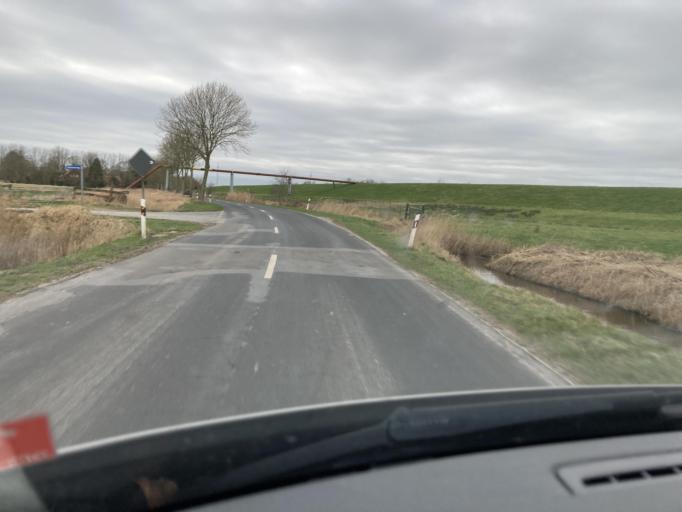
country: DE
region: Lower Saxony
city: Leer
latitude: 53.2115
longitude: 7.4531
